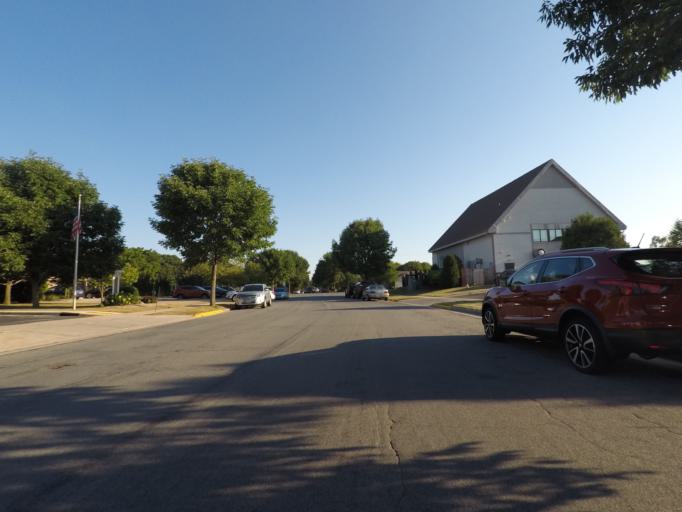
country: US
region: Wisconsin
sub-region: Dane County
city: Verona
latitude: 43.0023
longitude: -89.5294
